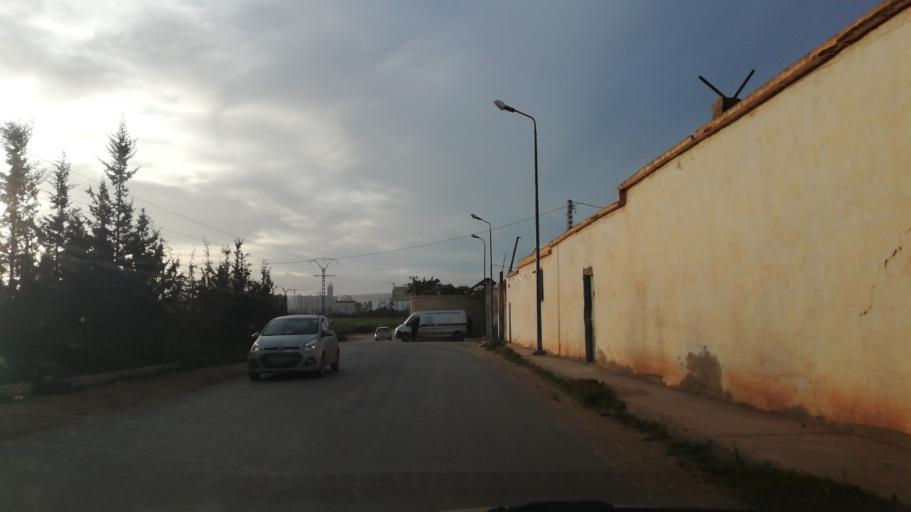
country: DZ
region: Oran
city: Es Senia
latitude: 35.6790
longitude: -0.5897
